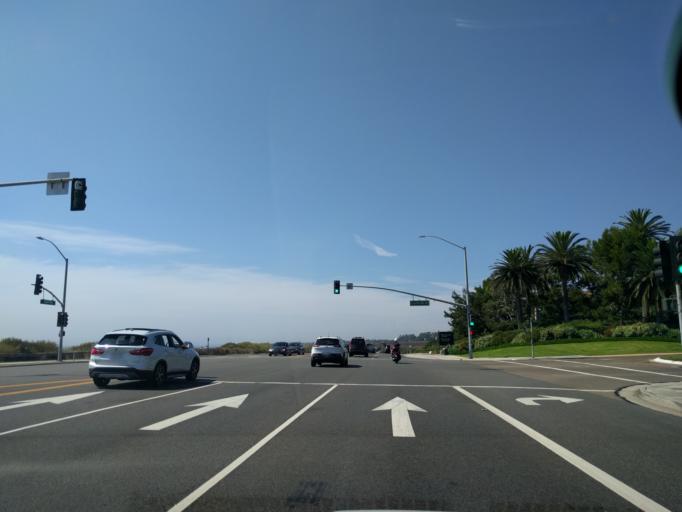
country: US
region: California
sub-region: Orange County
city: San Joaquin Hills
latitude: 33.5710
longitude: -117.8356
